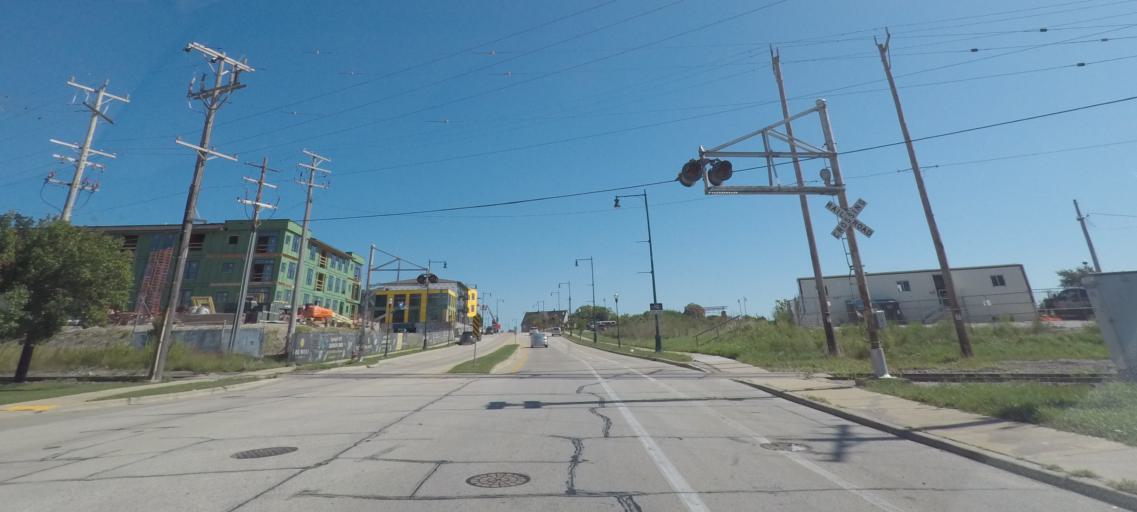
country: US
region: Wisconsin
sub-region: Milwaukee County
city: West Allis
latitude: 43.0141
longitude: -87.9966
